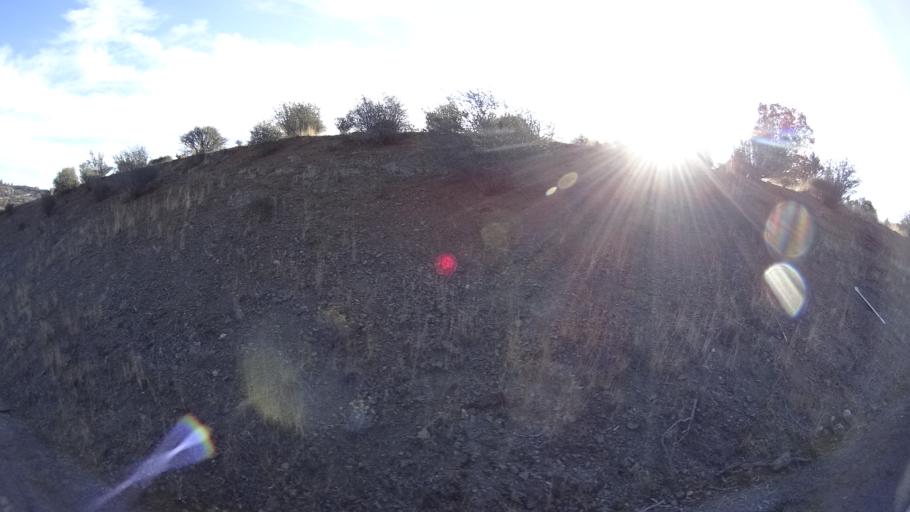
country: US
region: California
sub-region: Siskiyou County
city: Yreka
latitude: 41.7102
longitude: -122.6257
